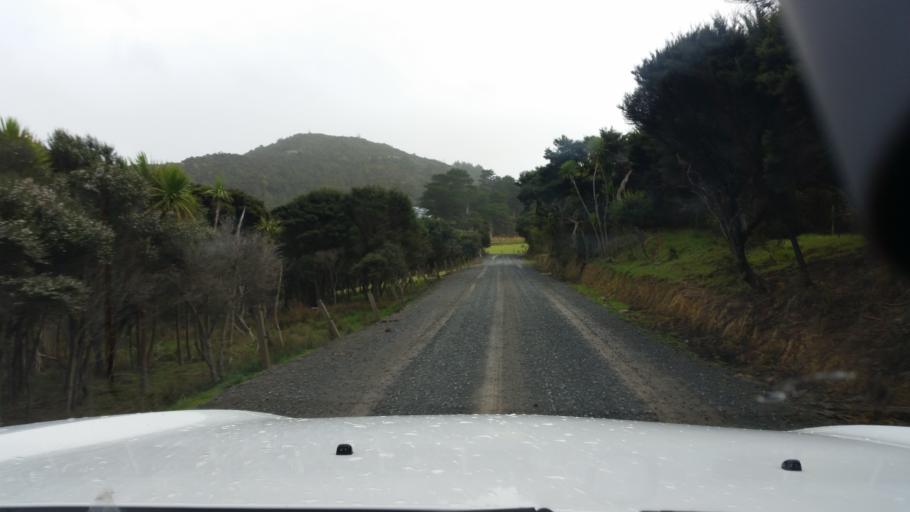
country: NZ
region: Northland
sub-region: Whangarei
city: Ruakaka
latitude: -35.7800
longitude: 174.5459
